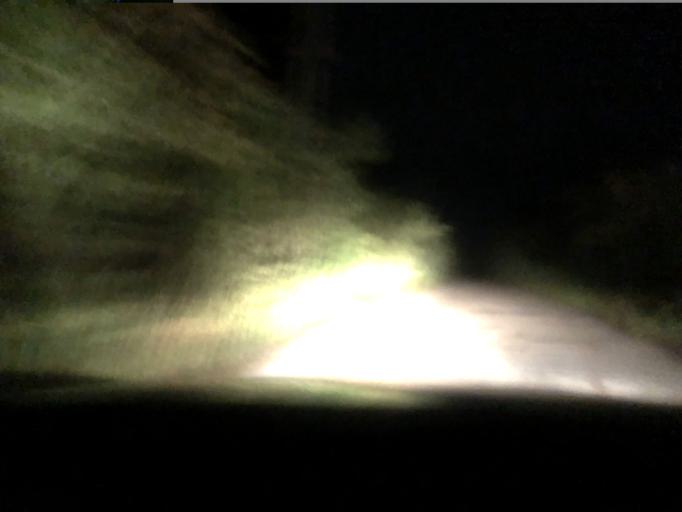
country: TH
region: Nakhon Sawan
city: Takhli
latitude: 15.2566
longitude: 100.3359
